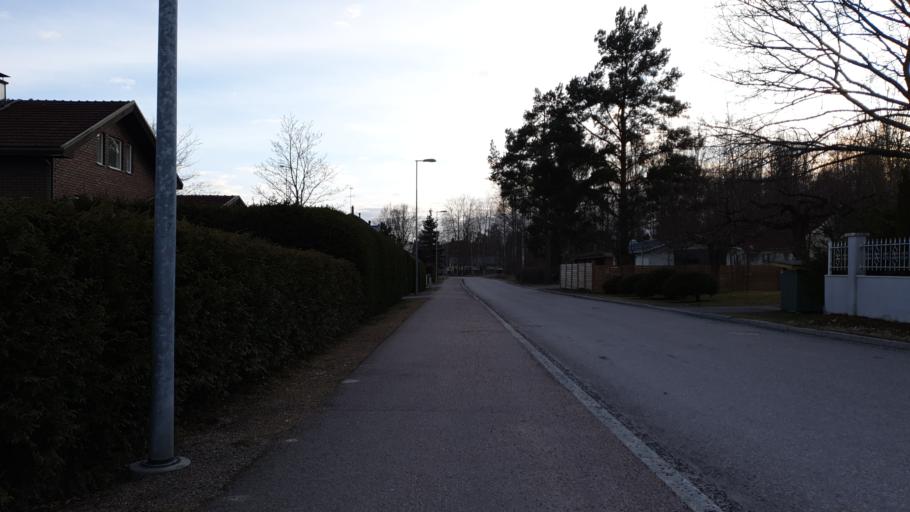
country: FI
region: Uusimaa
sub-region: Helsinki
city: Vantaa
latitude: 60.3141
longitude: 25.0108
